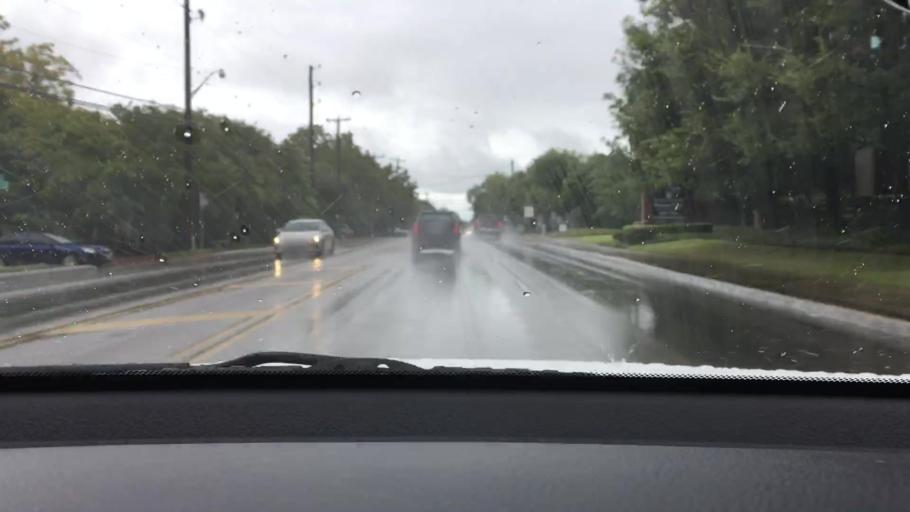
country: US
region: Texas
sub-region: Bexar County
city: Alamo Heights
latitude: 29.4960
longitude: -98.4666
